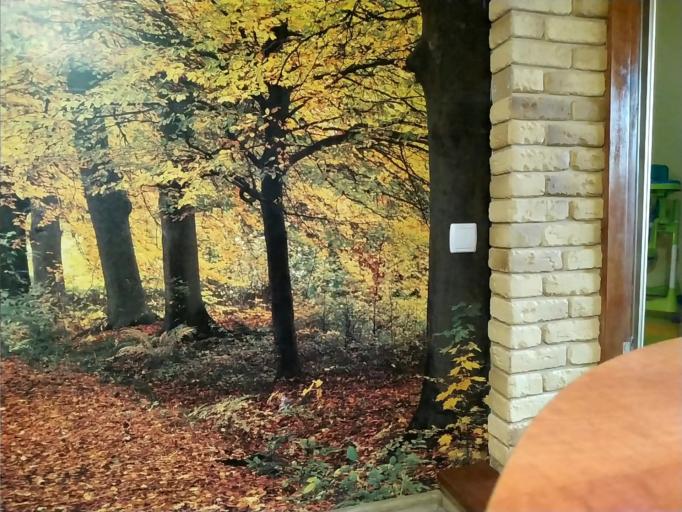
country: RU
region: Leningrad
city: Tolmachevo
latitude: 58.9282
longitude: 29.7277
